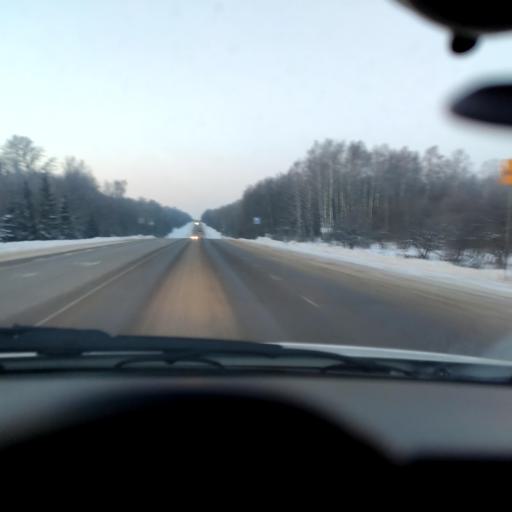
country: RU
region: Kursk
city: Zheleznogorsk
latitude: 52.3021
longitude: 35.3452
